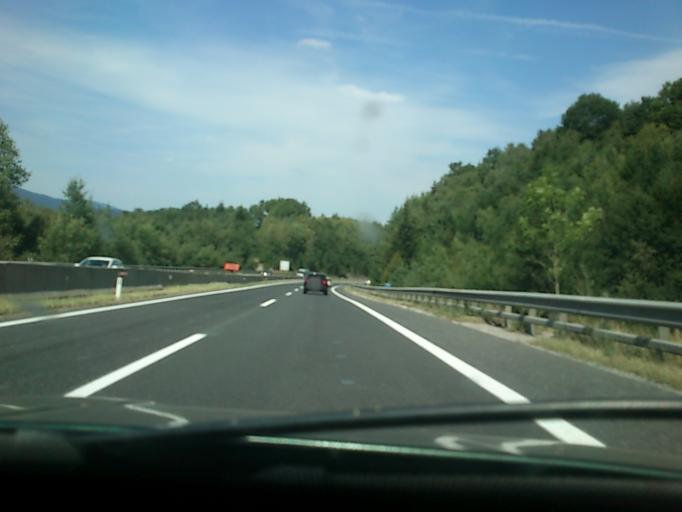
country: AT
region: Lower Austria
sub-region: Politischer Bezirk Neunkirchen
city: Thomasberg
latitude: 47.5631
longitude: 16.1190
